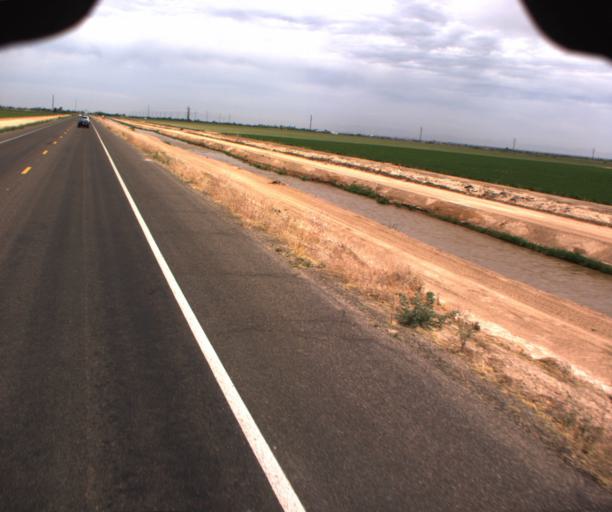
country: US
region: Arizona
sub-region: Pinal County
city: Eloy
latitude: 32.8527
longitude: -111.5153
